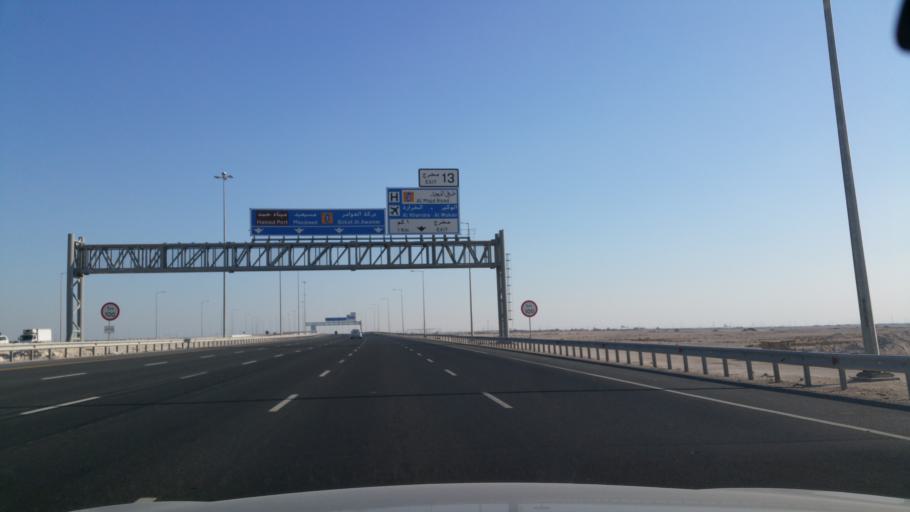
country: QA
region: Al Wakrah
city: Al Wukayr
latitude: 25.1397
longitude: 51.4763
